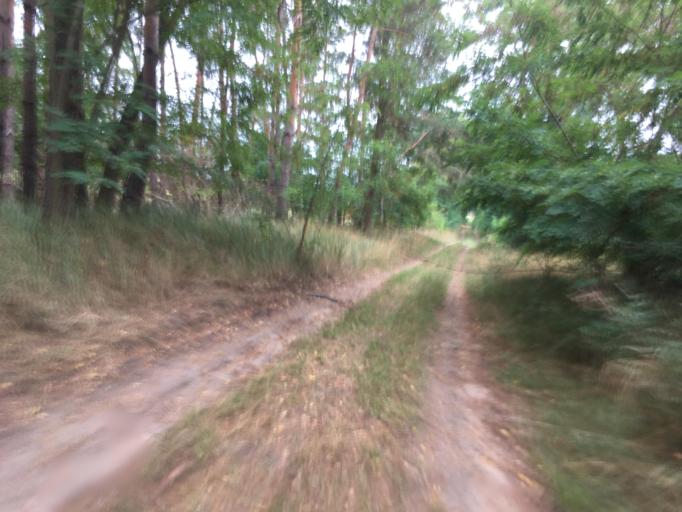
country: DE
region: Brandenburg
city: Passow
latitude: 53.1130
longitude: 14.1227
